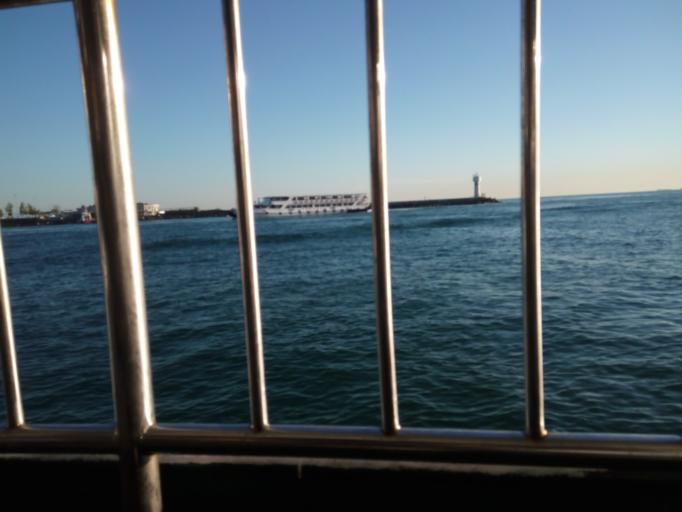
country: TR
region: Istanbul
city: UEskuedar
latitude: 40.9941
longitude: 29.0171
